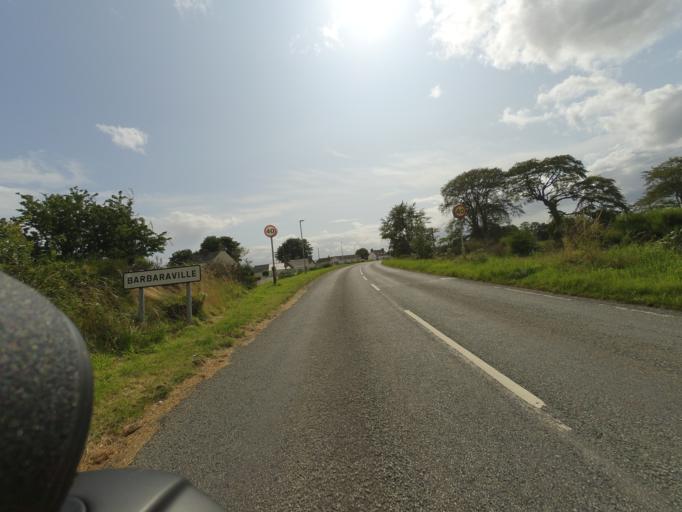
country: GB
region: Scotland
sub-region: Highland
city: Invergordon
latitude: 57.7255
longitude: -4.0968
